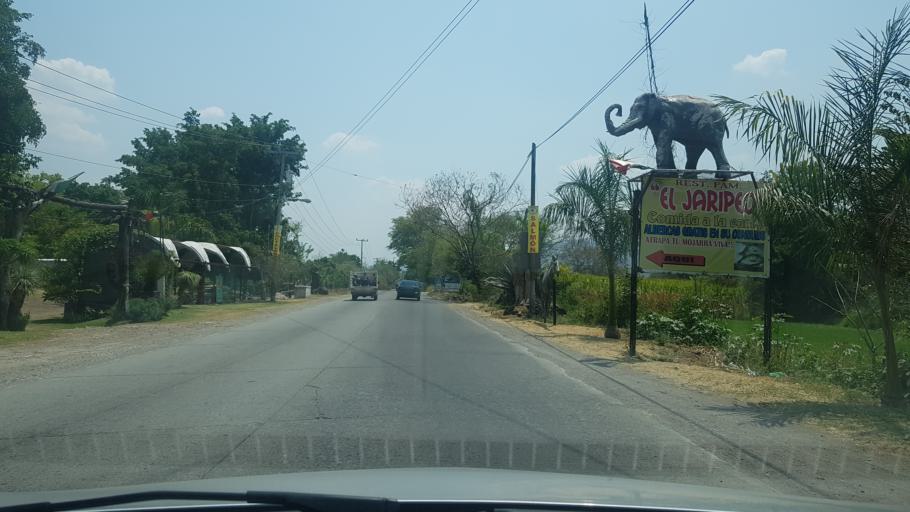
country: MX
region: Morelos
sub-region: Jiutepec
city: Independencia
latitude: 18.7992
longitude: -99.1013
